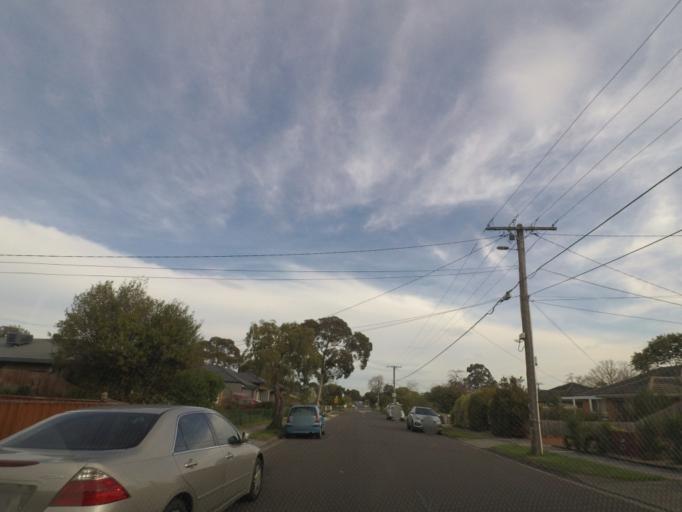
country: AU
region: Victoria
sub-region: Knox
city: Knoxfield
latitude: -37.8930
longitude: 145.2405
